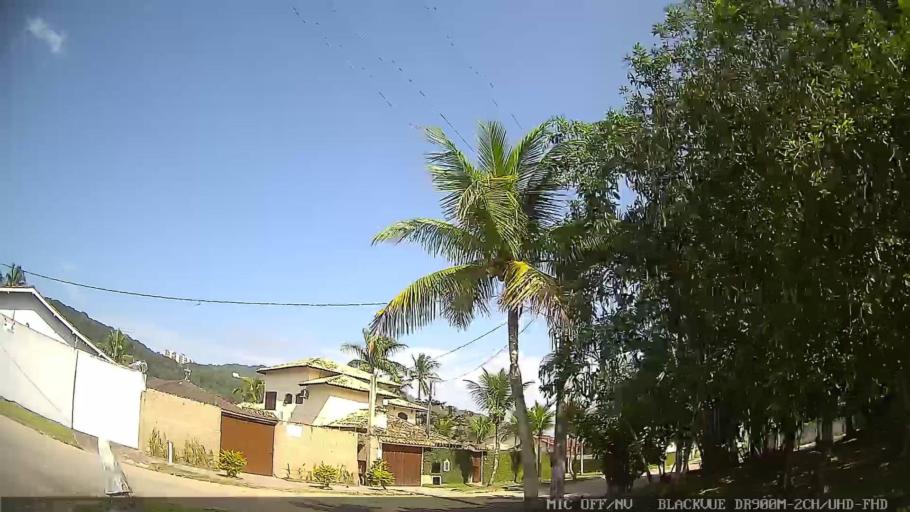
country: BR
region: Sao Paulo
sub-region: Guaruja
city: Guaruja
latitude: -23.9740
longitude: -46.1903
